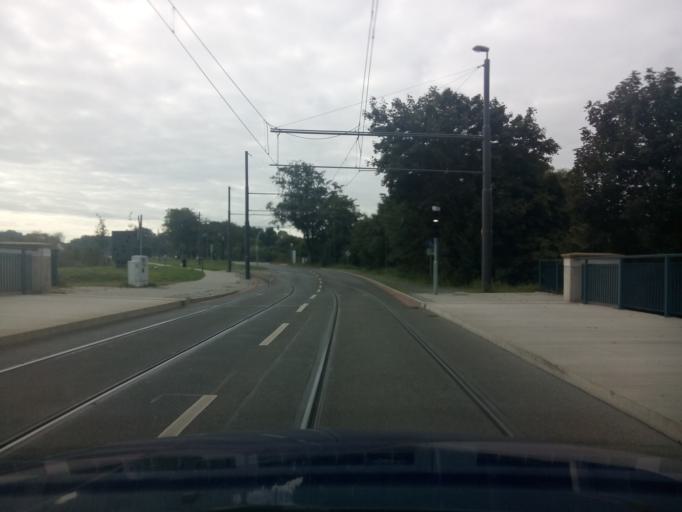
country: DE
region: Lower Saxony
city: Lilienthal
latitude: 53.1340
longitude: 8.8982
